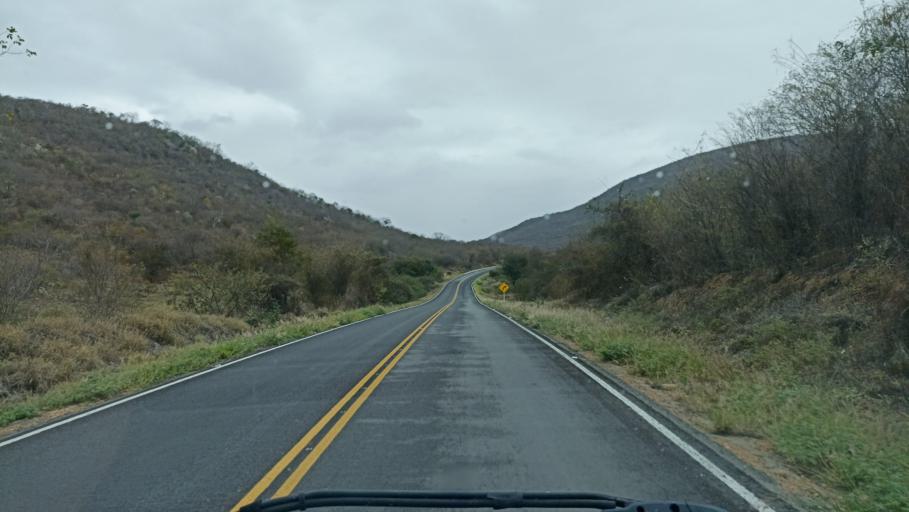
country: BR
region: Bahia
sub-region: Andarai
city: Vera Cruz
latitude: -13.0476
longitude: -40.7784
